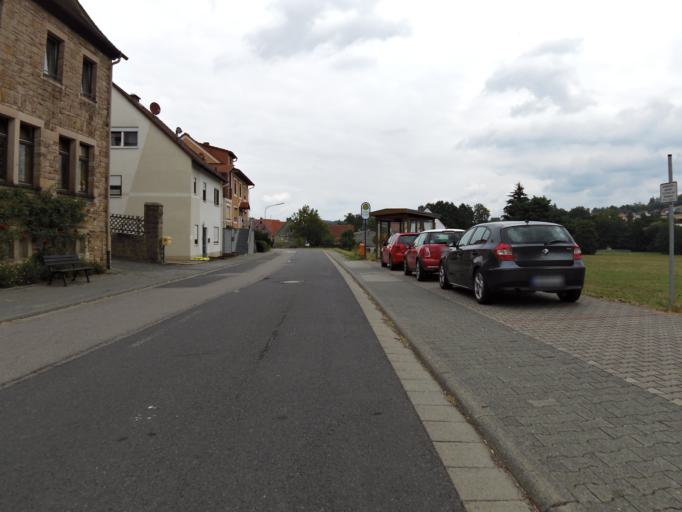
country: DE
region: Hesse
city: Reichelsheim
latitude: 49.7028
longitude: 8.8232
